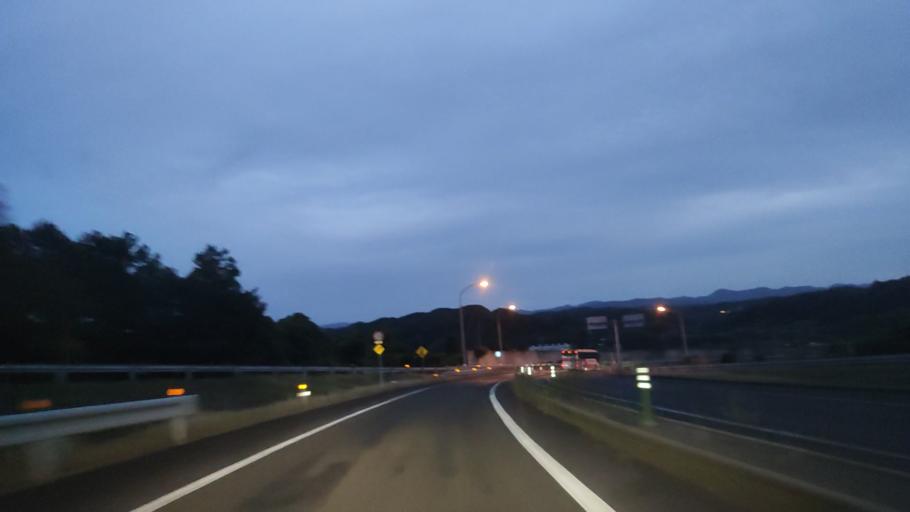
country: JP
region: Hyogo
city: Sandacho
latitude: 34.8895
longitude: 135.1173
